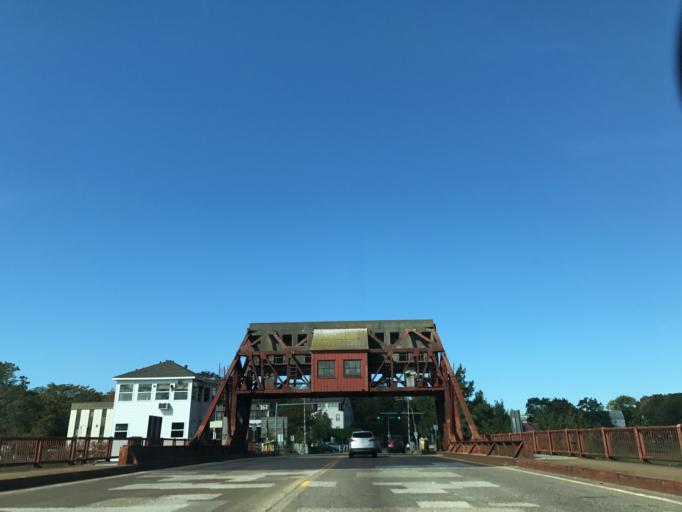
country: US
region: Massachusetts
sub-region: Norfolk County
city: Milton
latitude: 42.2771
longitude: -71.0529
